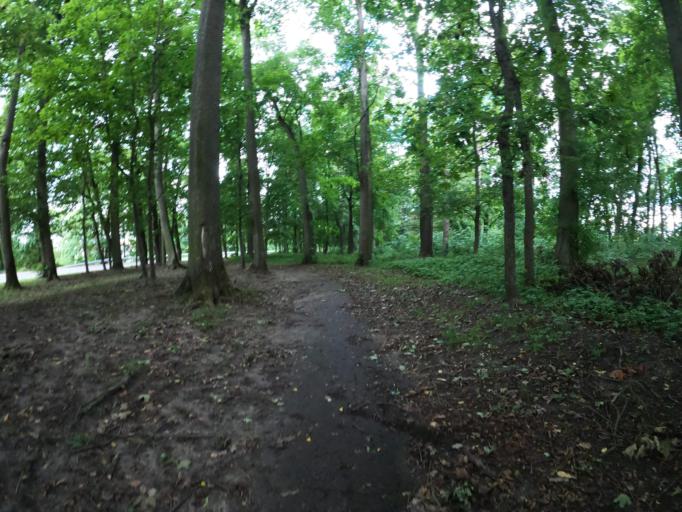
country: RU
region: Kaliningrad
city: Zheleznodorozhnyy
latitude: 54.3612
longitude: 21.3126
